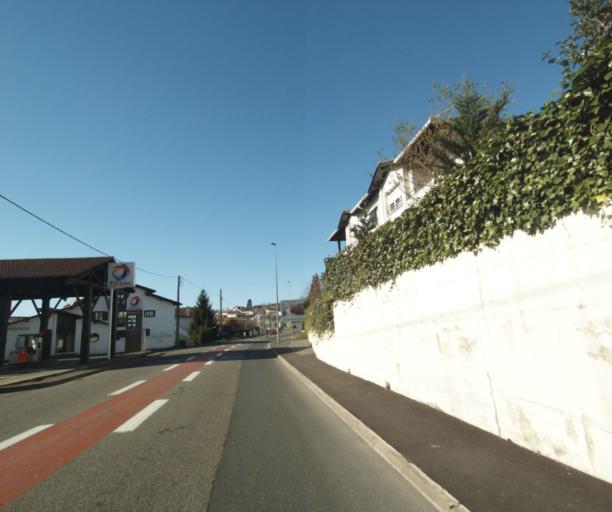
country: ES
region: Basque Country
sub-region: Provincia de Guipuzcoa
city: Irun
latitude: 43.3469
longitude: -1.7660
